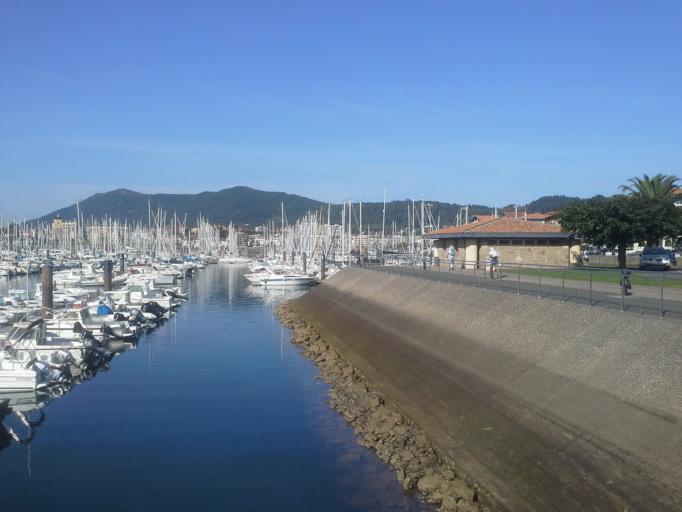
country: FR
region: Aquitaine
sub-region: Departement des Pyrenees-Atlantiques
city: Hendaye
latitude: 43.3703
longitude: -1.7813
